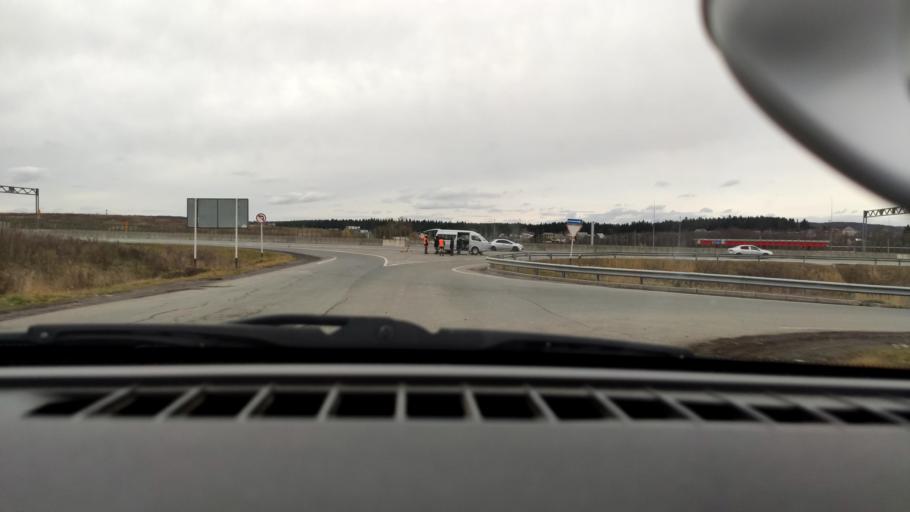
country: RU
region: Perm
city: Ferma
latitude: 57.9299
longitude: 56.3300
